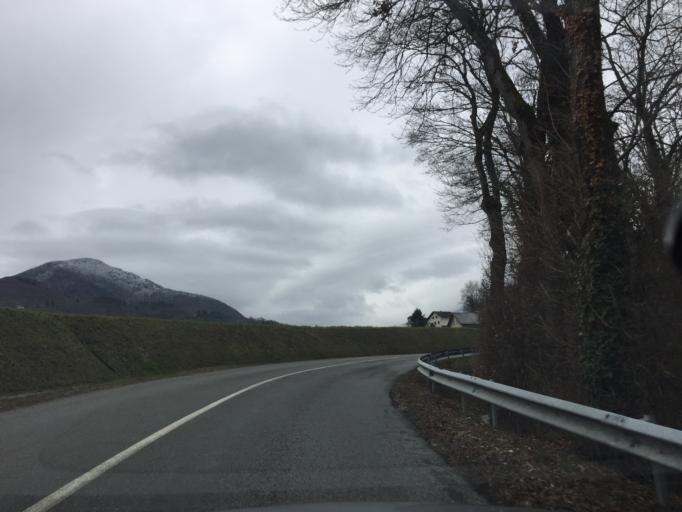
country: FR
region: Rhone-Alpes
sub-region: Departement de la Savoie
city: Cognin
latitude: 45.5510
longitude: 5.8860
